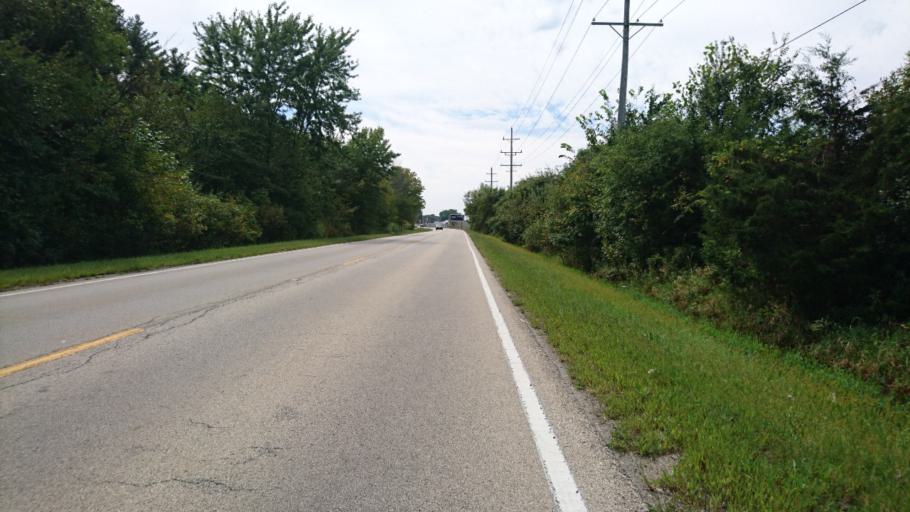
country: US
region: Illinois
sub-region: Will County
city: Braidwood
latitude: 41.2688
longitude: -88.2058
